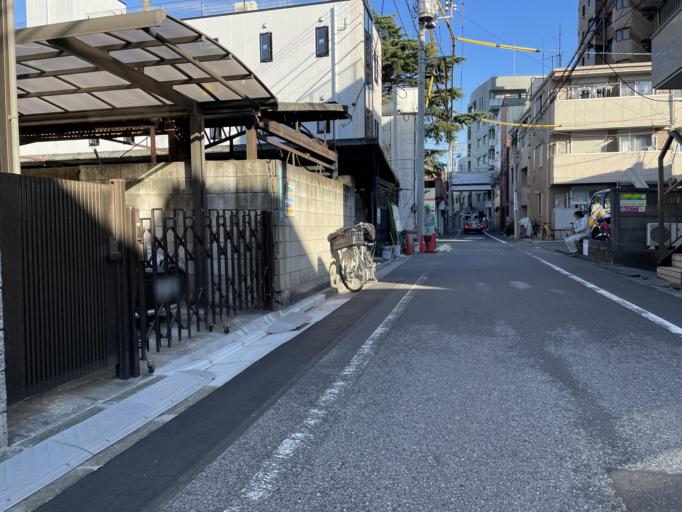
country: JP
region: Tokyo
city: Urayasu
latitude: 35.7281
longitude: 139.8810
